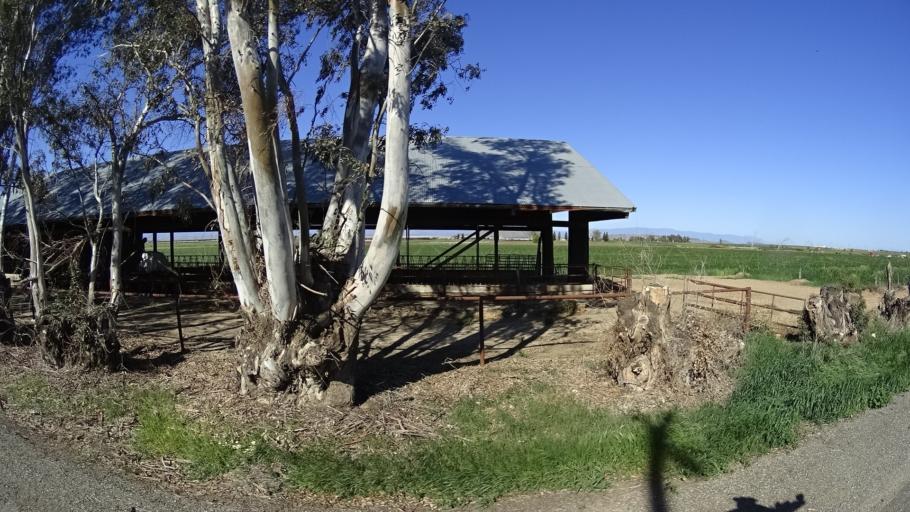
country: US
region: California
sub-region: Glenn County
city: Orland
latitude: 39.7385
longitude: -122.2481
